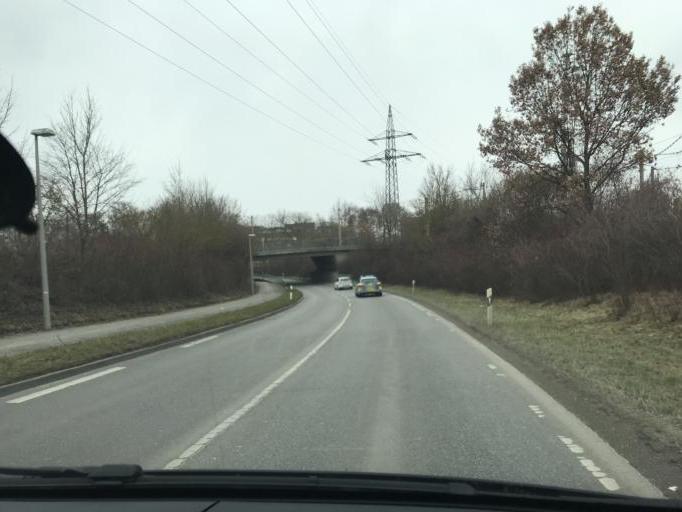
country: DE
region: Baden-Wuerttemberg
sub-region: Regierungsbezirk Stuttgart
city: Leinfelden-Echterdingen
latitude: 48.7239
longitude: 9.1321
